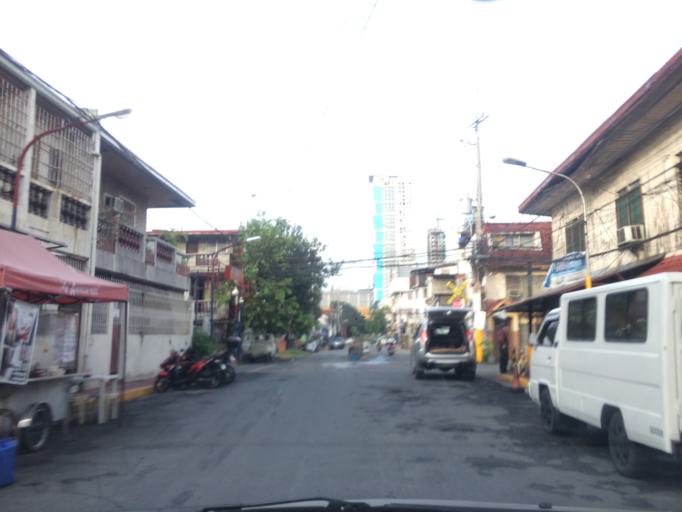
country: PH
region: Metro Manila
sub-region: City of Manila
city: Manila
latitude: 14.6154
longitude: 120.9945
